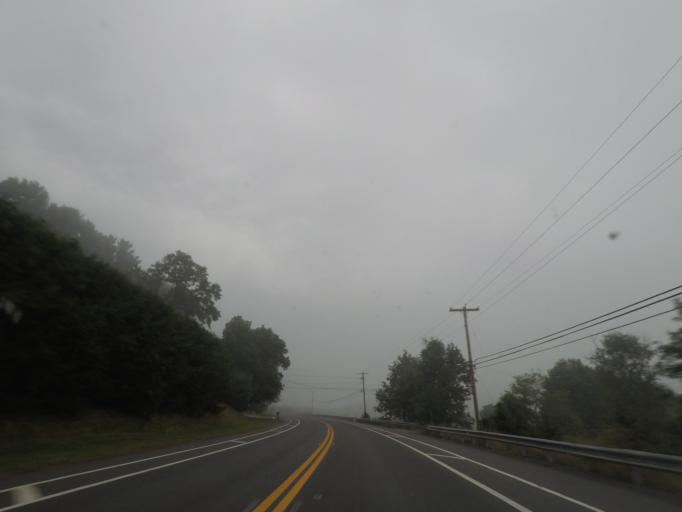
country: US
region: Massachusetts
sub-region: Hampden County
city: Palmer
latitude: 42.1470
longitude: -72.2741
